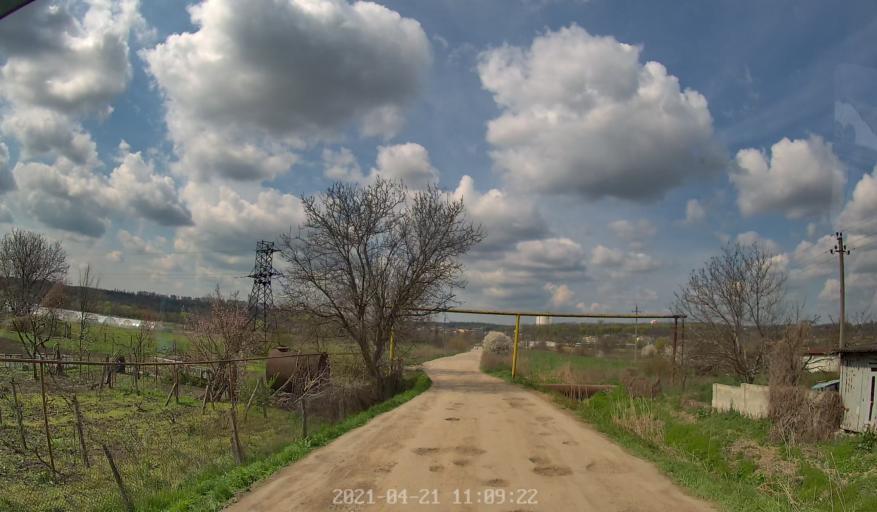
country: MD
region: Chisinau
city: Singera
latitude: 46.9577
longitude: 28.9399
